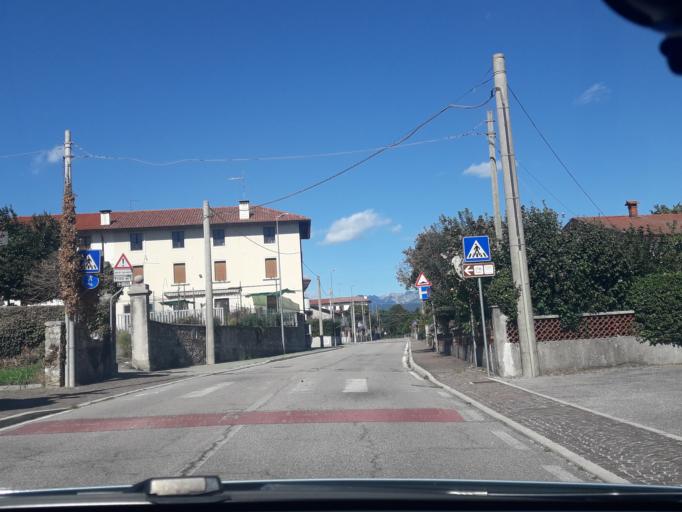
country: IT
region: Friuli Venezia Giulia
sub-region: Provincia di Udine
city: Reana del Roiale
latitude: 46.1293
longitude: 13.2151
